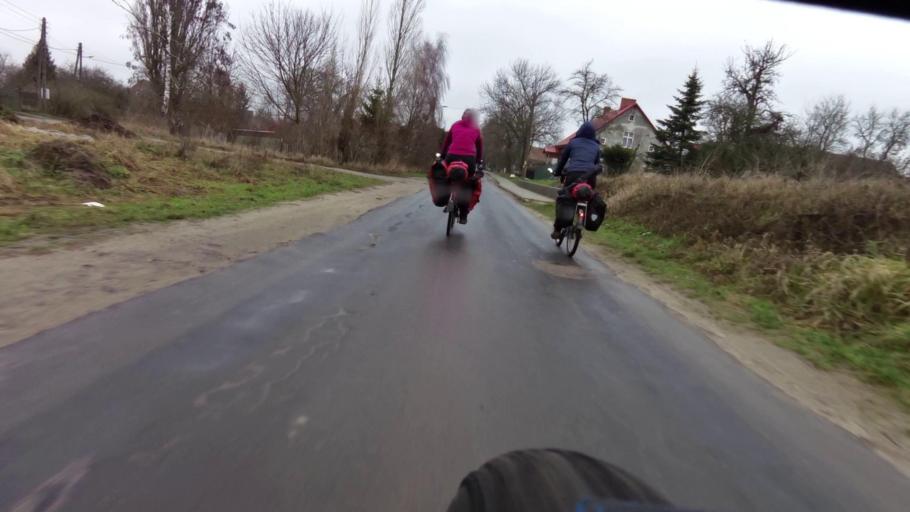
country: PL
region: West Pomeranian Voivodeship
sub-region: Powiat mysliborski
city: Debno
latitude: 52.6503
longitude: 14.7173
